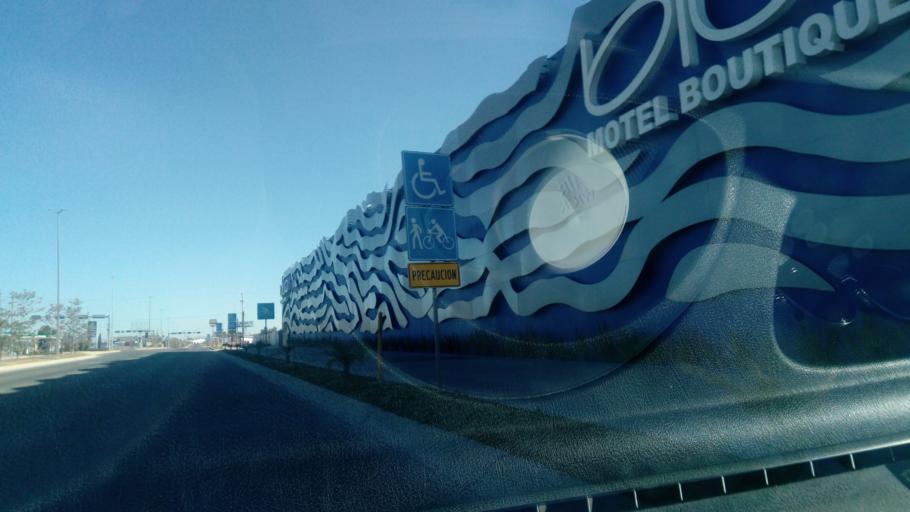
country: MX
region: Durango
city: Victoria de Durango
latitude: 24.0836
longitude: -104.5851
